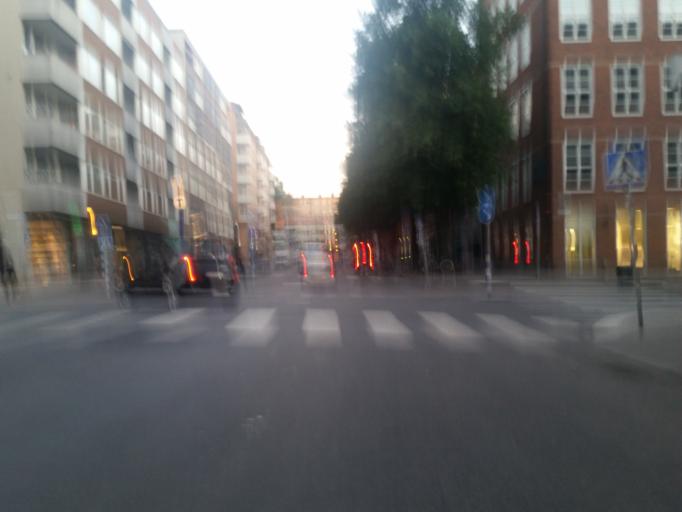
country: SE
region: Stockholm
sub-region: Stockholms Kommun
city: Stockholm
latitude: 59.3177
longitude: 18.0572
